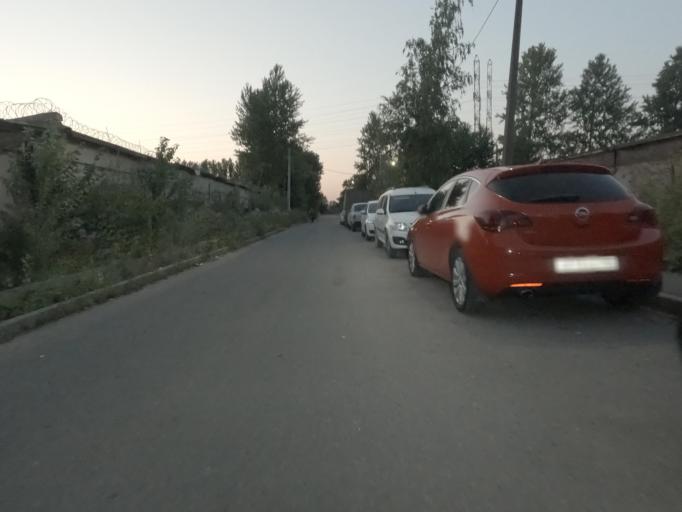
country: RU
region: St.-Petersburg
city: Avtovo
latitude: 59.8730
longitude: 30.2860
